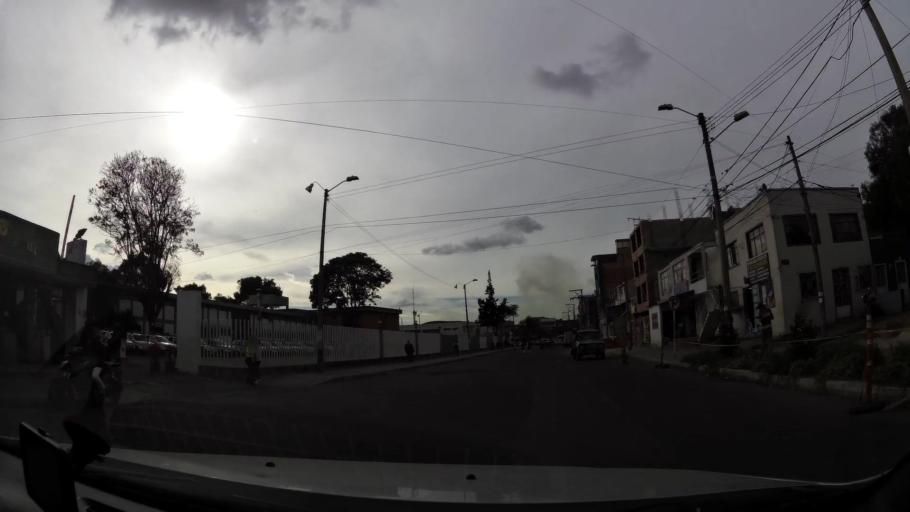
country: CO
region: Cundinamarca
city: Soacha
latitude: 4.6197
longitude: -74.1589
